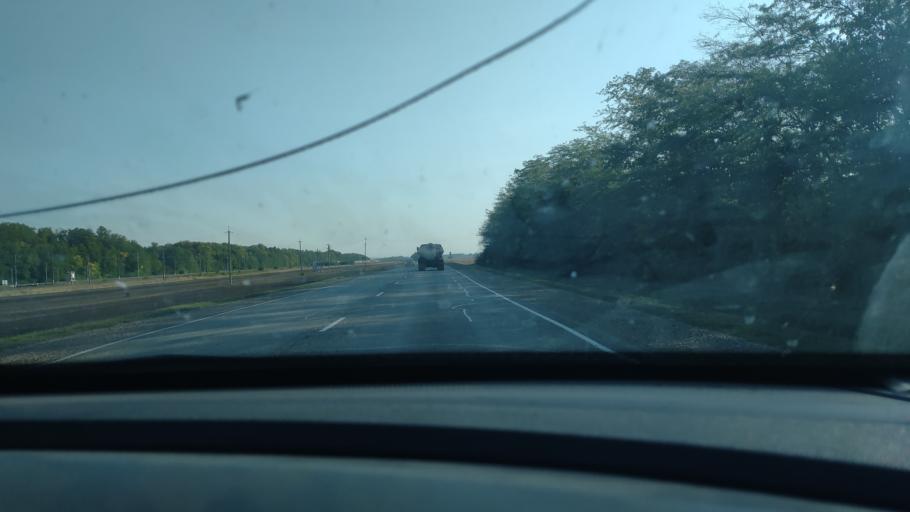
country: RU
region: Krasnodarskiy
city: Starominskaya
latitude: 46.4803
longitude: 39.0510
